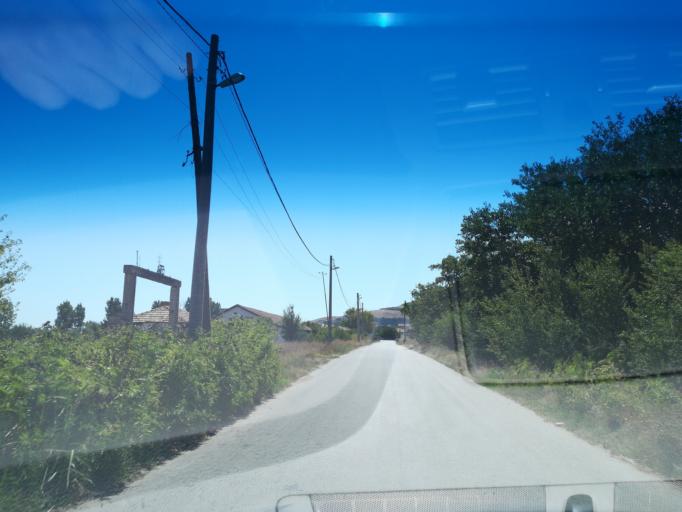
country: BG
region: Pazardzhik
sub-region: Obshtina Pazardzhik
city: Pazardzhik
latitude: 42.3428
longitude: 24.4005
